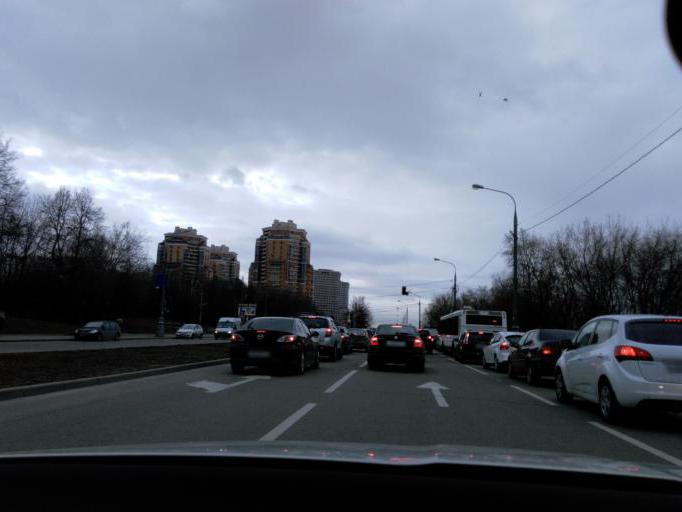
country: RU
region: Moscow
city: Golovinskiy
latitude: 55.8598
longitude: 37.4881
